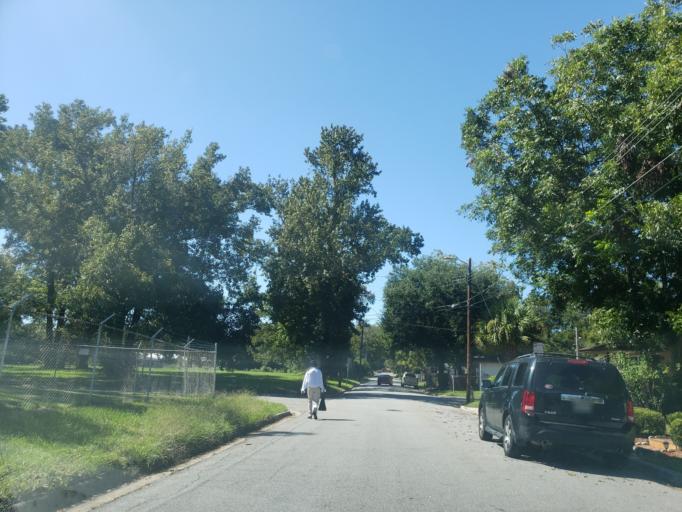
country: US
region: Georgia
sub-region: Chatham County
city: Savannah
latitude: 32.0498
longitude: -81.1119
